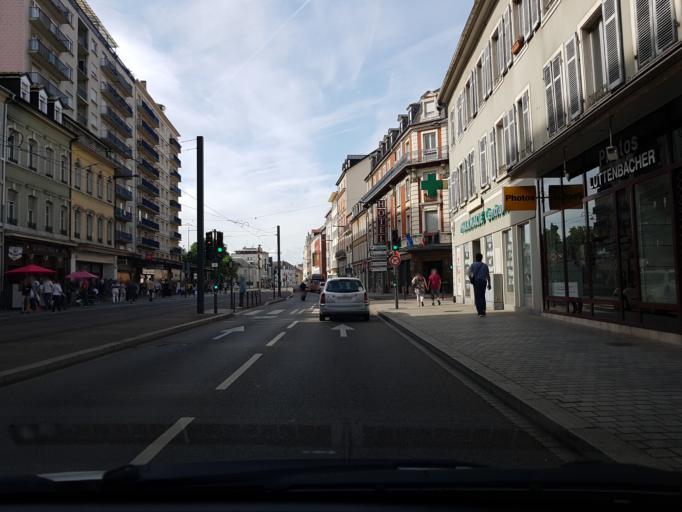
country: FR
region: Alsace
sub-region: Departement du Haut-Rhin
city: Mulhouse
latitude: 47.7512
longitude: 7.3383
